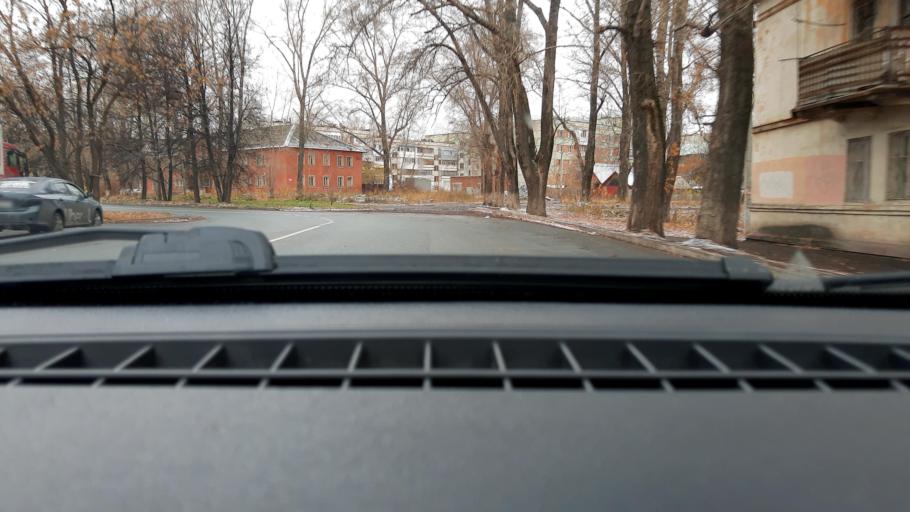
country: RU
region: Bashkortostan
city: Ufa
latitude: 54.8152
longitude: 56.1182
